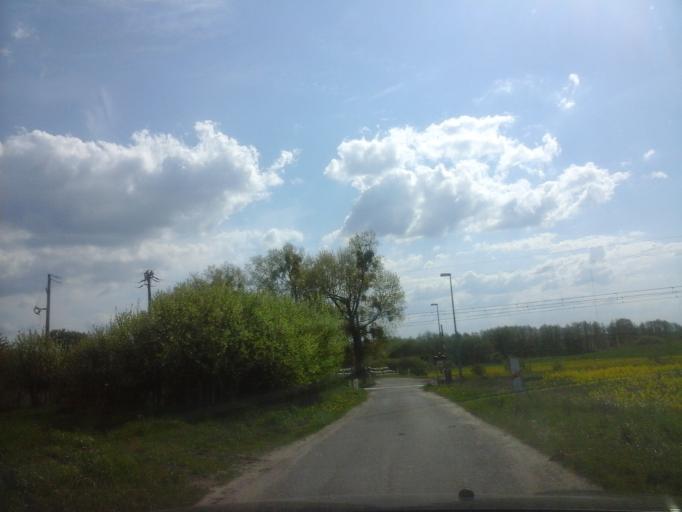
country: PL
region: West Pomeranian Voivodeship
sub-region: Powiat choszczenski
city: Krzecin
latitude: 53.1064
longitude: 15.4923
